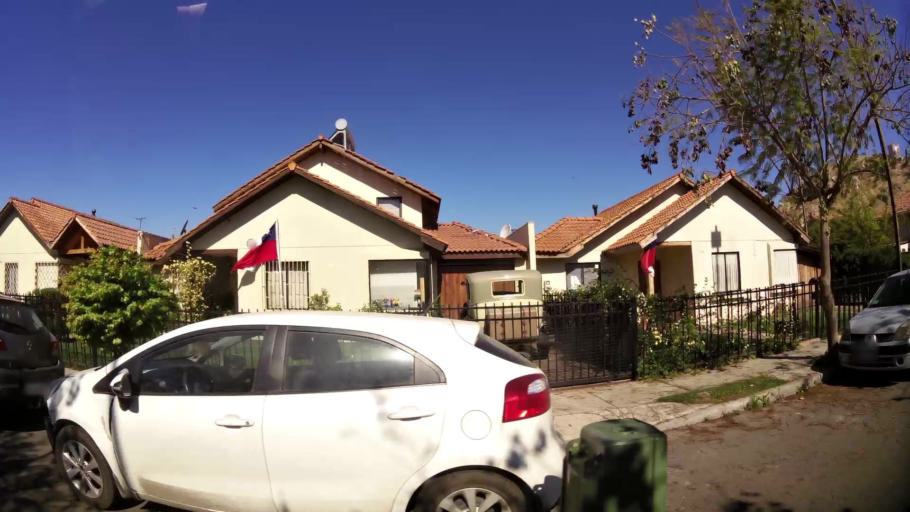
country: CL
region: Santiago Metropolitan
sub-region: Provincia de Talagante
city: Penaflor
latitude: -33.6050
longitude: -70.9070
